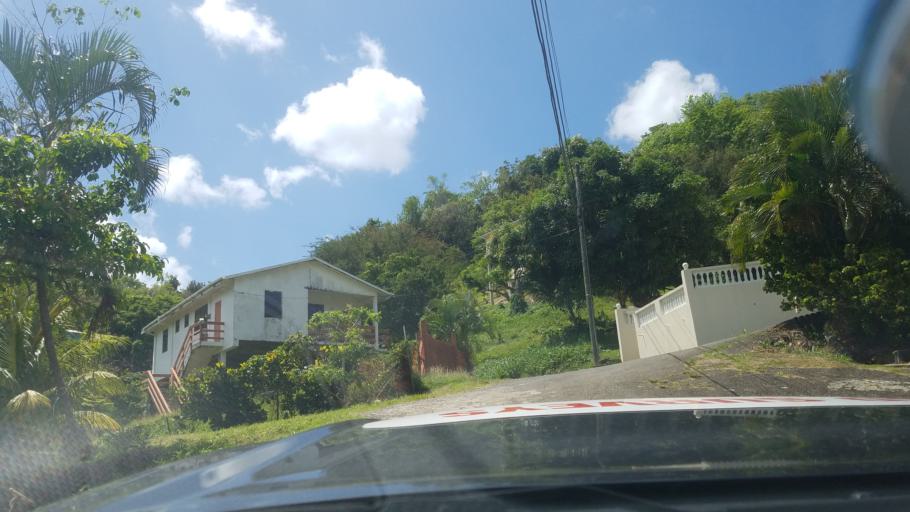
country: LC
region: Castries Quarter
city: Bisee
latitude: 14.0306
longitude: -60.9563
